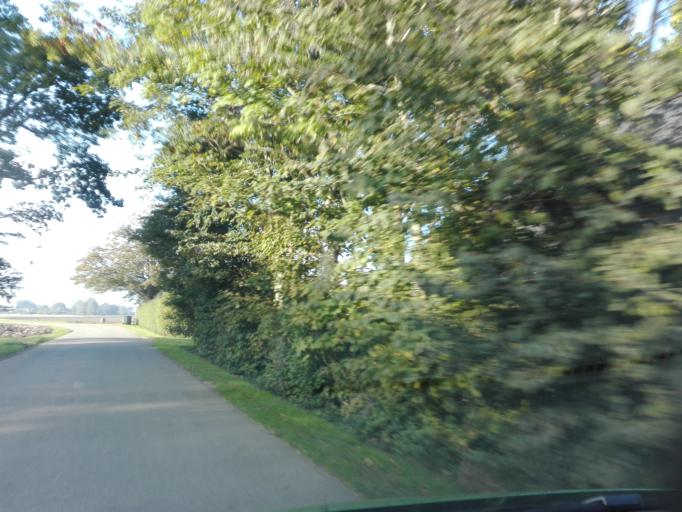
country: DK
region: Central Jutland
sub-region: Odder Kommune
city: Odder
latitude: 55.8995
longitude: 10.1965
